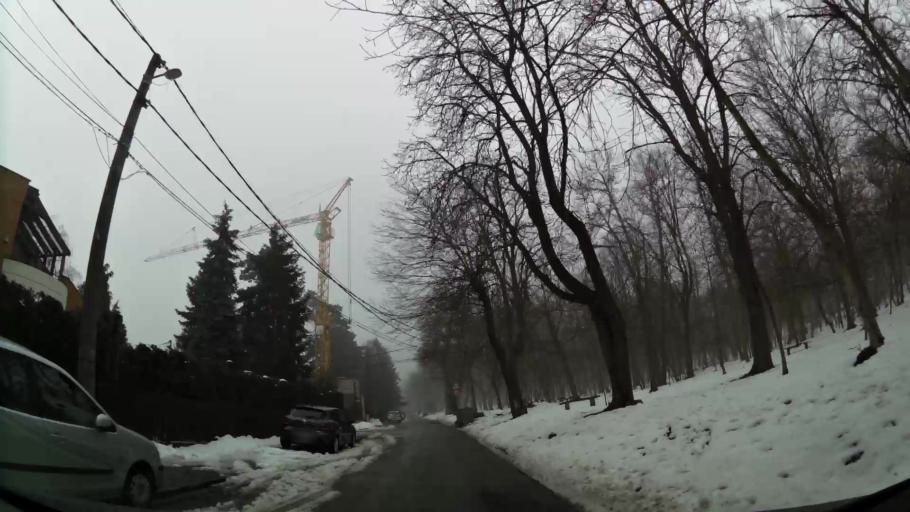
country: RS
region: Central Serbia
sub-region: Belgrade
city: Savski Venac
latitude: 44.7850
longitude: 20.4589
